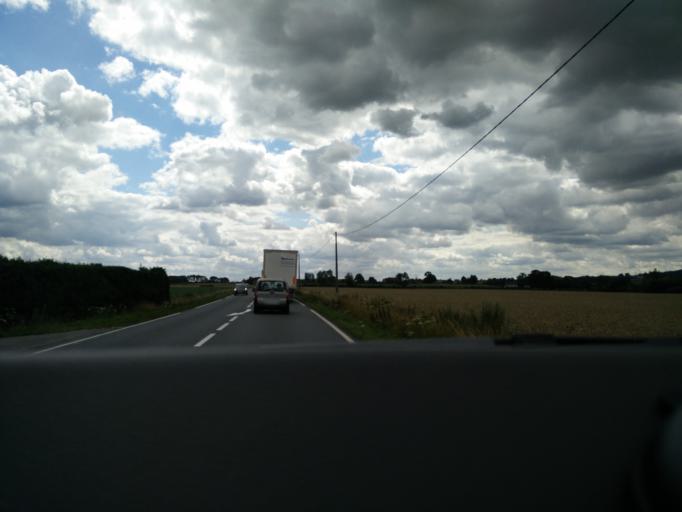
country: FR
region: Nord-Pas-de-Calais
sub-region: Departement du Nord
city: Steenvoorde
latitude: 50.8021
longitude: 2.5740
